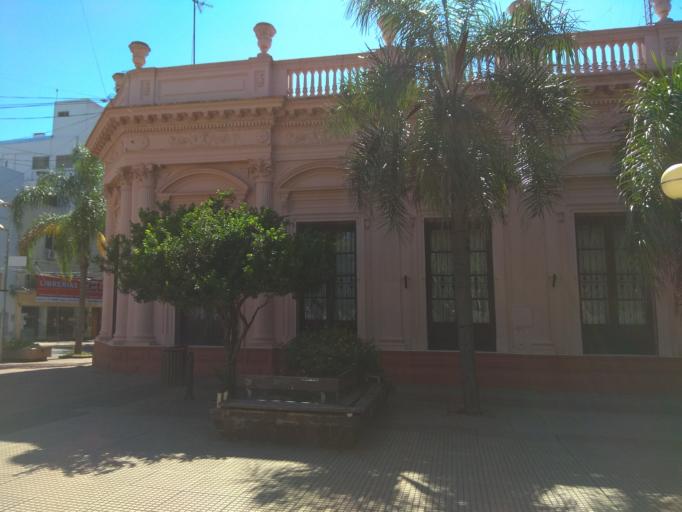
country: AR
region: Misiones
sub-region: Departamento de Capital
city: Posadas
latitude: -27.3662
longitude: -55.8935
